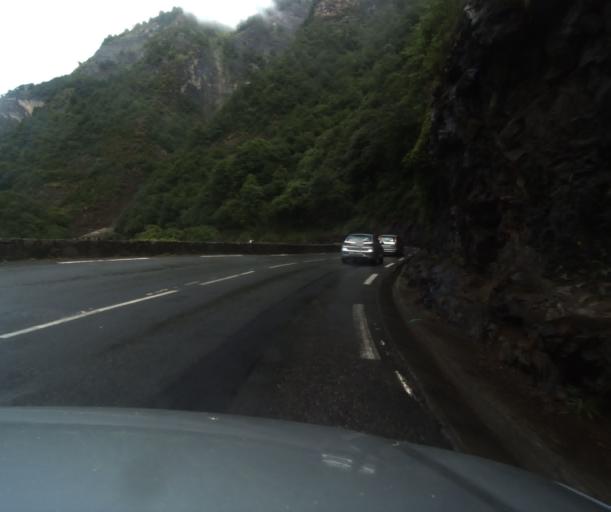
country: FR
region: Midi-Pyrenees
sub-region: Departement des Hautes-Pyrenees
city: Pierrefitte-Nestalas
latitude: 42.9258
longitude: -0.0421
